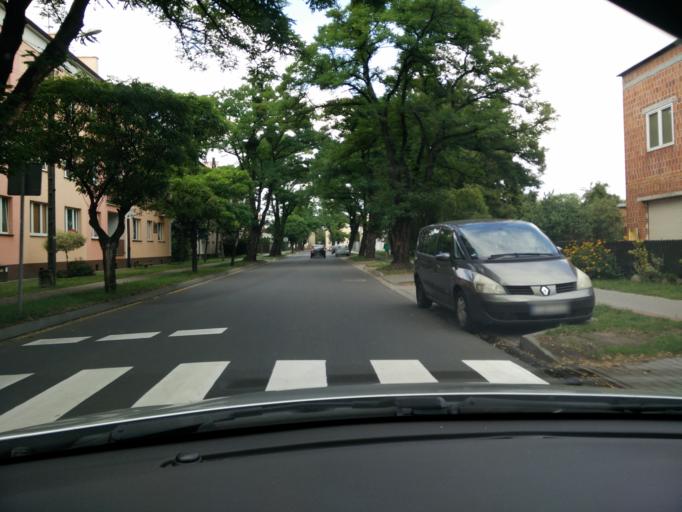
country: PL
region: Greater Poland Voivodeship
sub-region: Powiat sredzki
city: Sroda Wielkopolska
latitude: 52.2239
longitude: 17.2822
